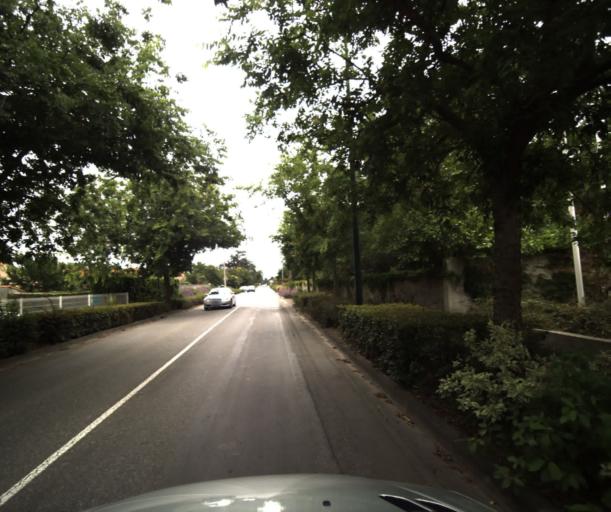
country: FR
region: Midi-Pyrenees
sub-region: Departement de la Haute-Garonne
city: Pinsaguel
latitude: 43.5001
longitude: 1.3923
